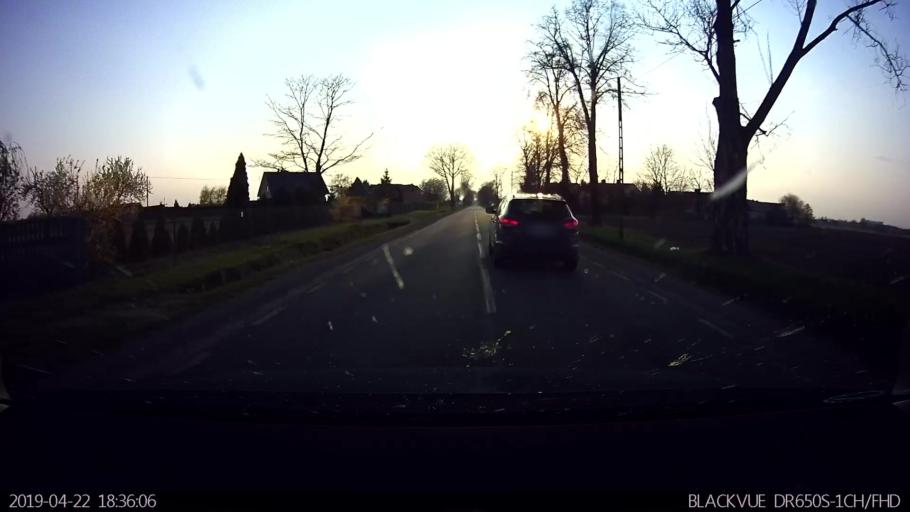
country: PL
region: Masovian Voivodeship
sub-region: Powiat wolominski
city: Klembow
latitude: 52.4455
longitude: 21.3349
